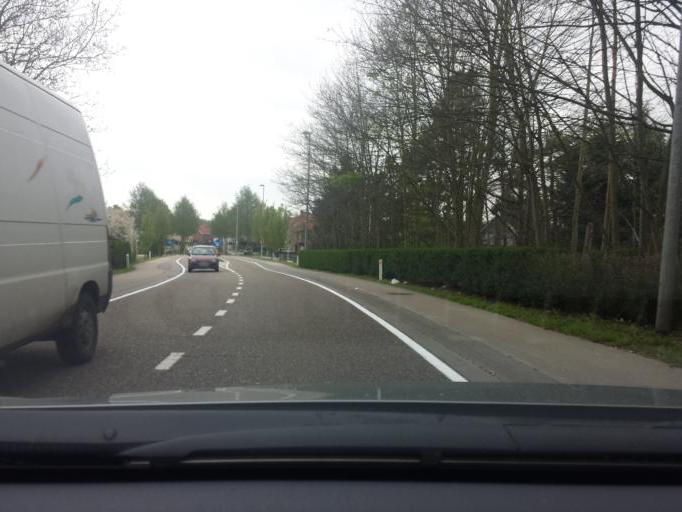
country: BE
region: Flanders
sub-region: Provincie Limburg
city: Beringen
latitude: 51.0438
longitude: 5.2156
